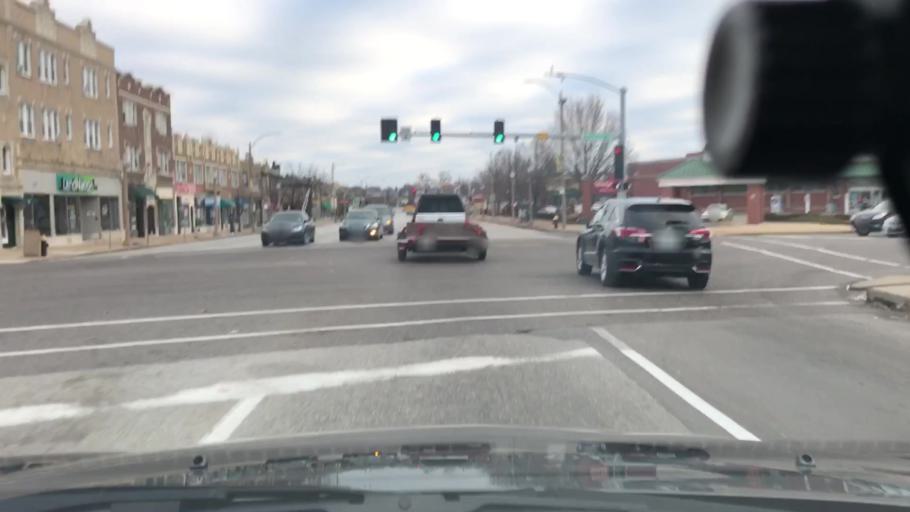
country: US
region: Missouri
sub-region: Saint Louis County
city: Maplewood
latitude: 38.5913
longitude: -90.2734
